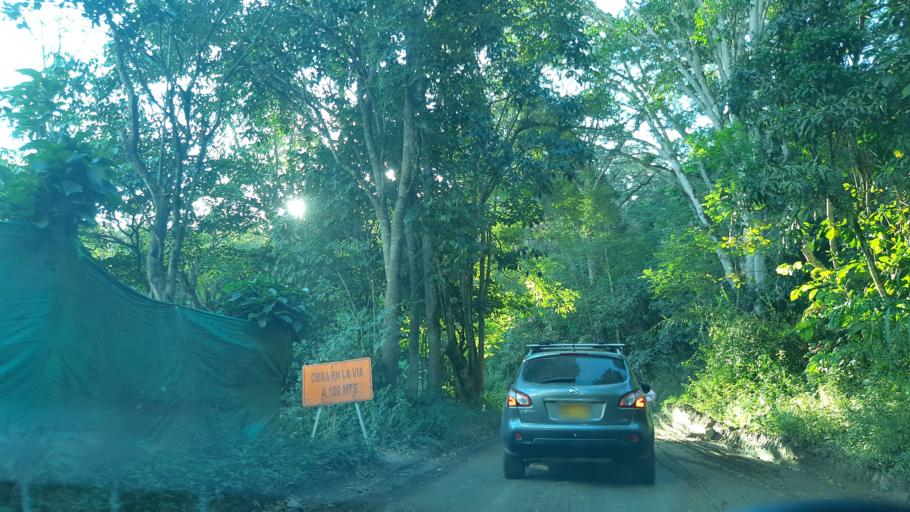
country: CO
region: Boyaca
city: Garagoa
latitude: 5.0812
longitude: -73.3909
